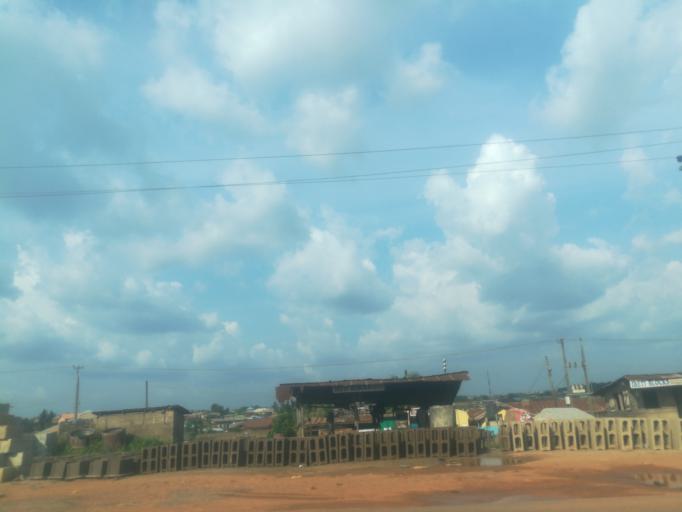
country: NG
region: Oyo
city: Ido
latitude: 7.3984
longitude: 3.8066
